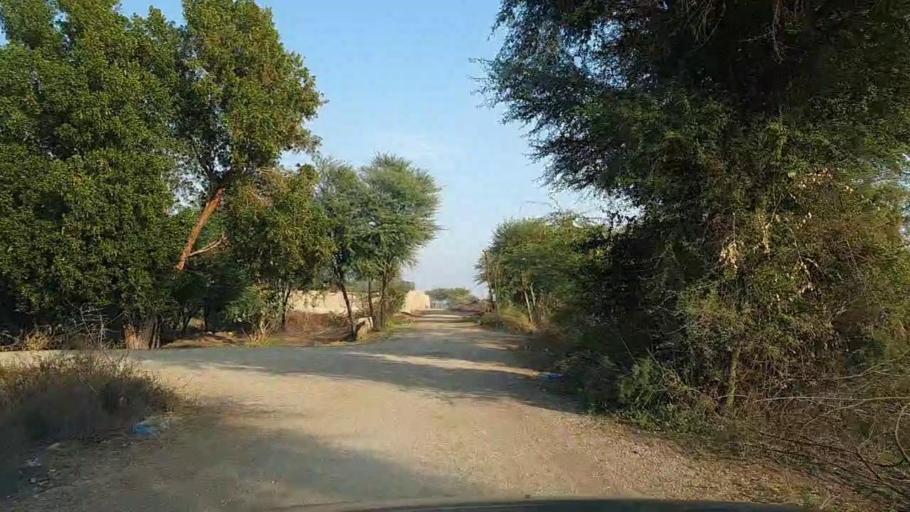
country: PK
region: Sindh
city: Jam Sahib
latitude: 26.3640
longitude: 68.5365
